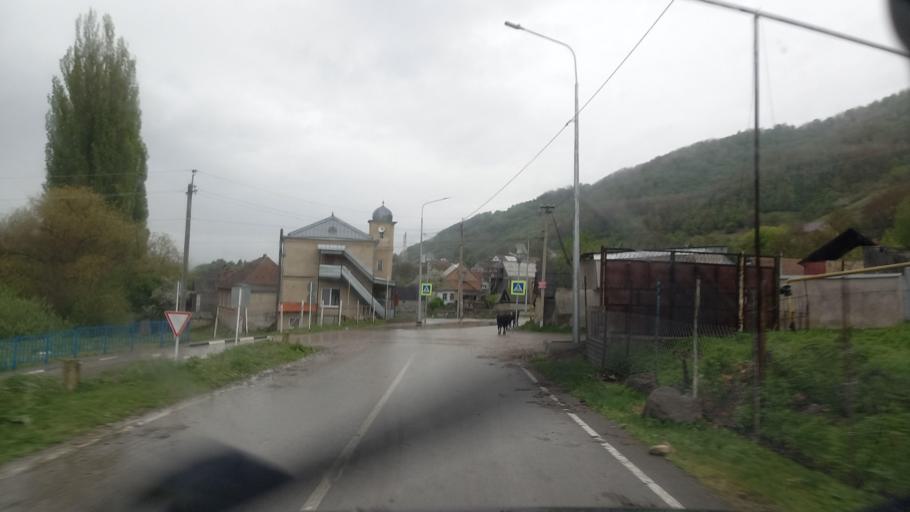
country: RU
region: Kabardino-Balkariya
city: Gundelen
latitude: 43.5965
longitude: 43.1528
